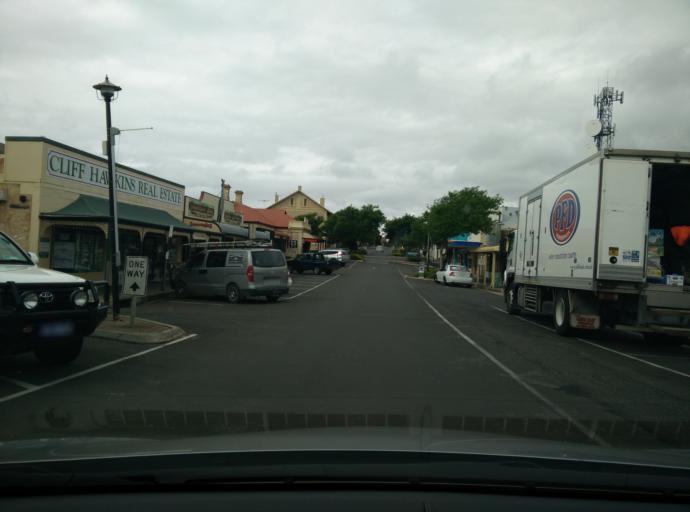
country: AU
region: South Australia
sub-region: Kangaroo Island
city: Kingscote
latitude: -35.6553
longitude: 137.6397
